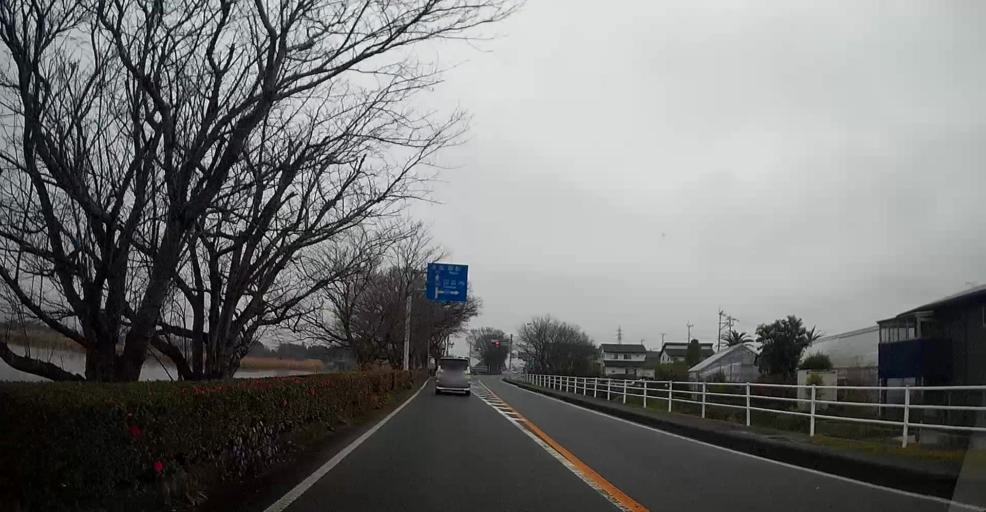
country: JP
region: Kumamoto
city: Kumamoto
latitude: 32.7672
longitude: 130.7510
